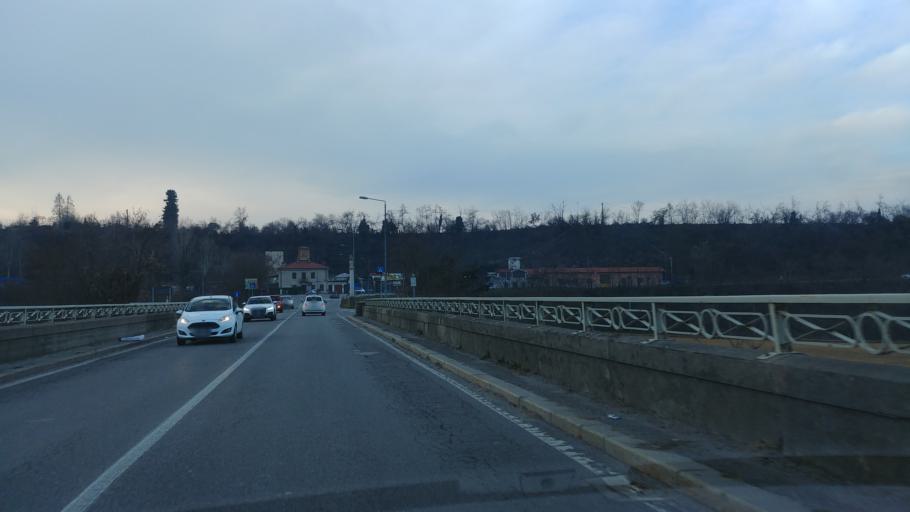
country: IT
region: Piedmont
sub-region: Provincia di Cuneo
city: Cuneo
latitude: 44.3989
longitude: 7.5455
